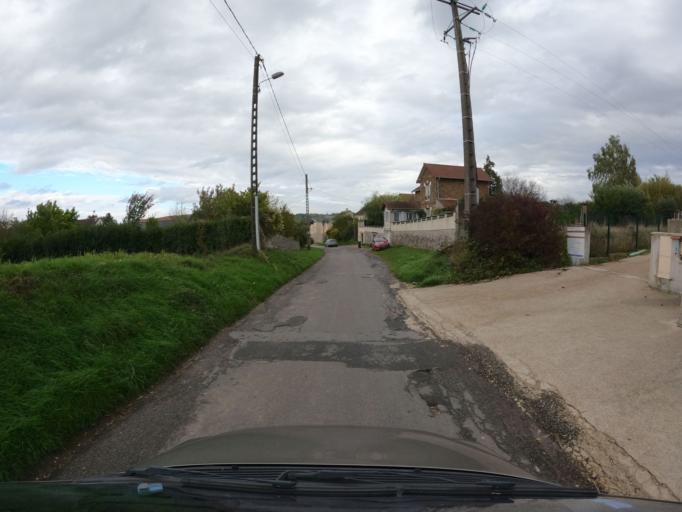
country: FR
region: Ile-de-France
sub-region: Departement de Seine-et-Marne
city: Saint-Germain-sur-Morin
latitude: 48.8765
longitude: 2.8500
